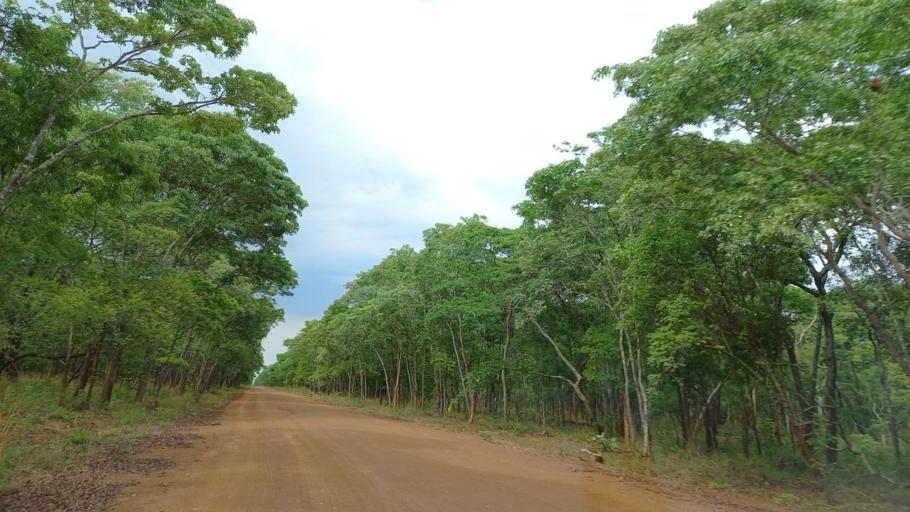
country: ZM
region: North-Western
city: Kalengwa
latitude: -13.4204
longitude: 25.0551
